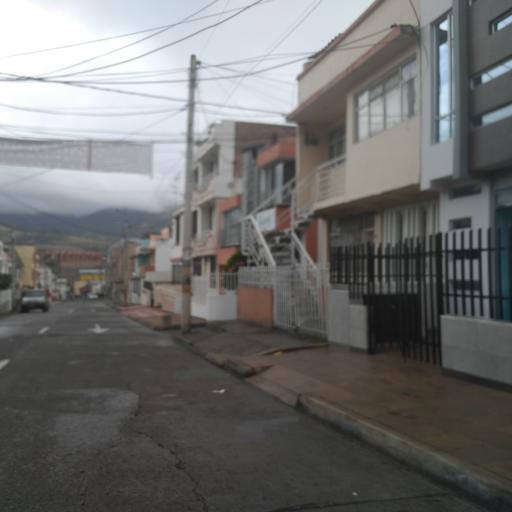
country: CO
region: Narino
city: Pasto
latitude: 1.2150
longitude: -77.2853
